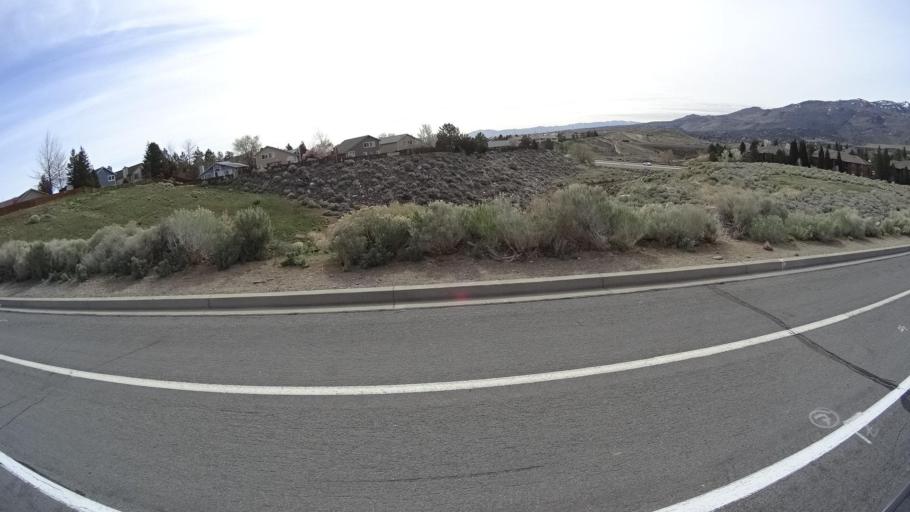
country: US
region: Nevada
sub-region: Washoe County
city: Mogul
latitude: 39.5233
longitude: -119.8974
